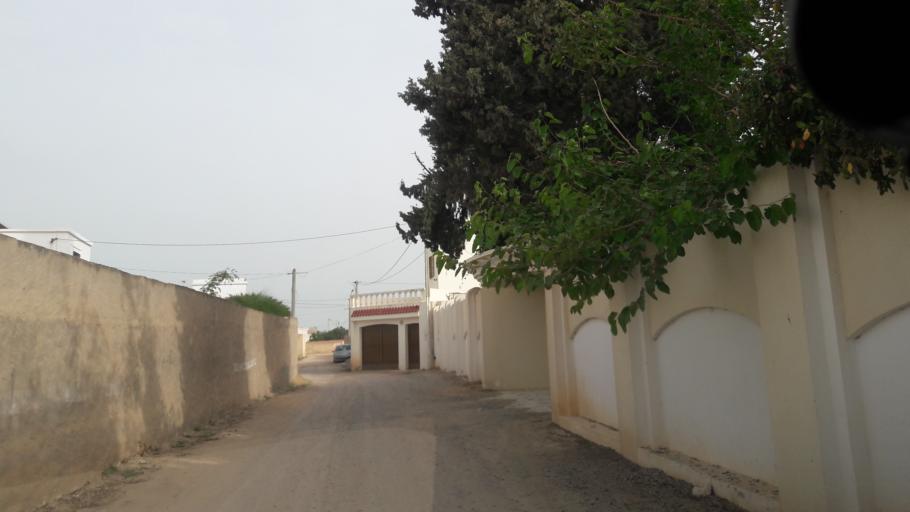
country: TN
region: Safaqis
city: Al Qarmadah
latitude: 34.7791
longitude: 10.7738
